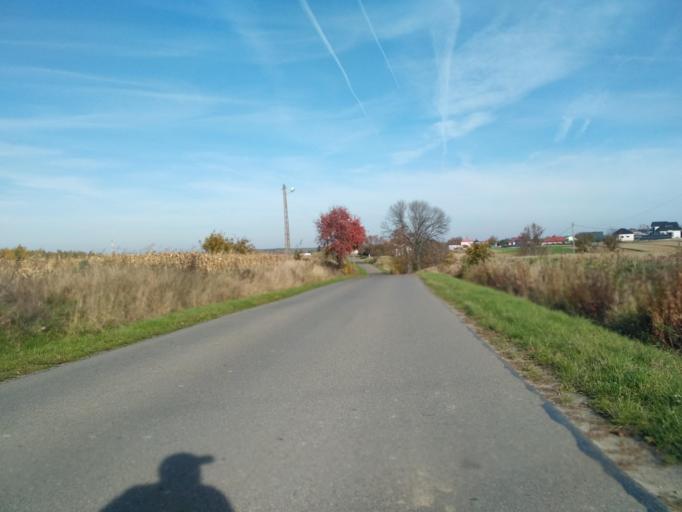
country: PL
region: Subcarpathian Voivodeship
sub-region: Powiat ropczycko-sedziszowski
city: Iwierzyce
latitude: 50.0581
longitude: 21.7802
